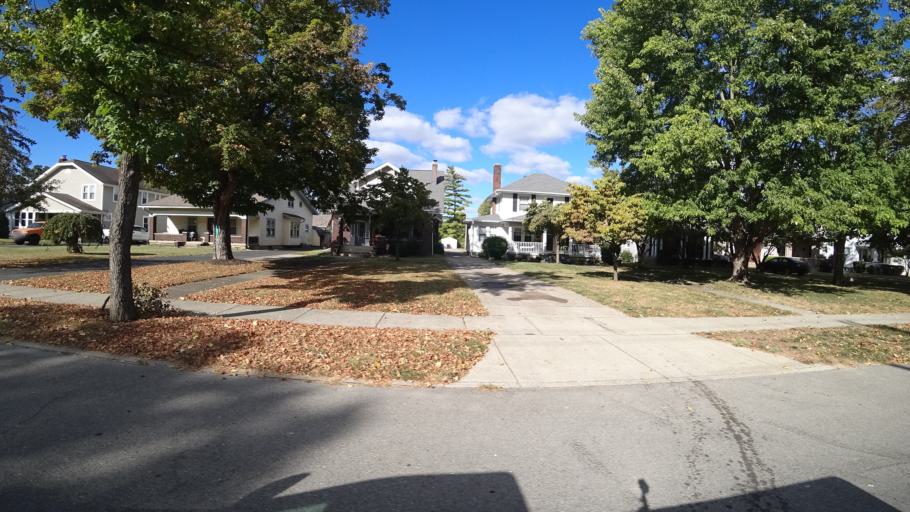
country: US
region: Ohio
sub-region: Butler County
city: Fairfield
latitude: 39.3651
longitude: -84.5578
